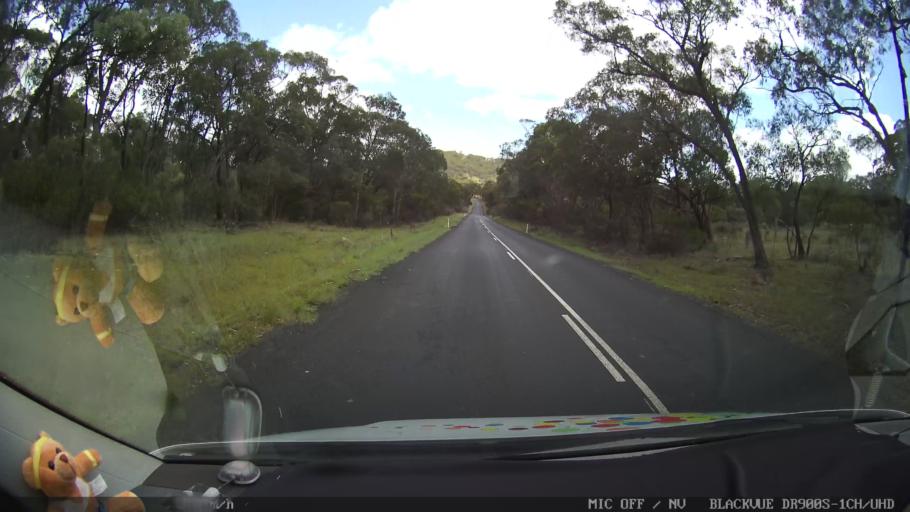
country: AU
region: New South Wales
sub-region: Glen Innes Severn
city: Glen Innes
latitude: -29.5420
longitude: 151.6697
